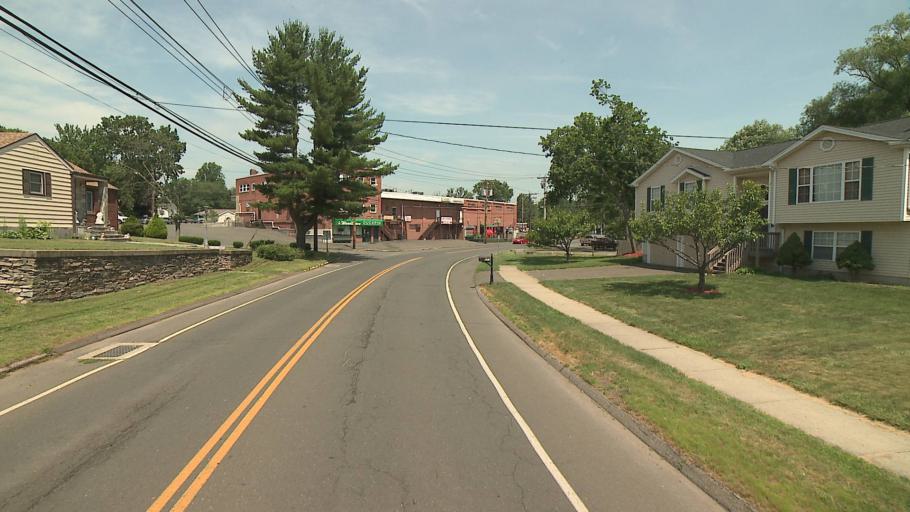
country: US
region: Connecticut
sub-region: New Haven County
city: West Haven
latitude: 41.2594
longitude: -72.9637
